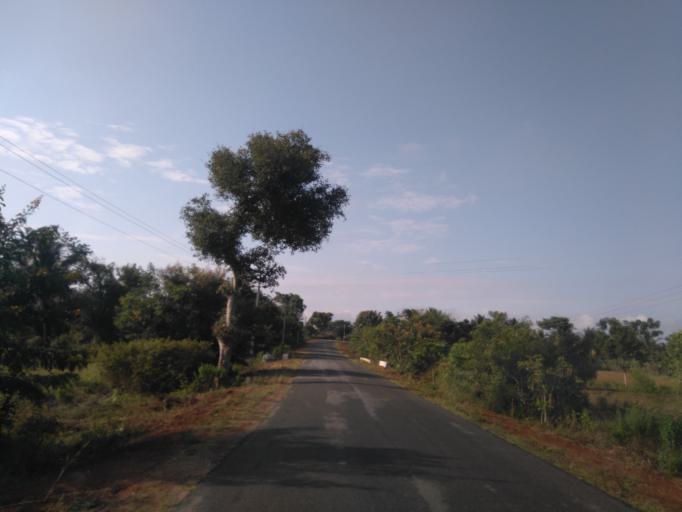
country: IN
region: Karnataka
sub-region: Mandya
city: Malavalli
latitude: 12.3160
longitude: 77.0719
